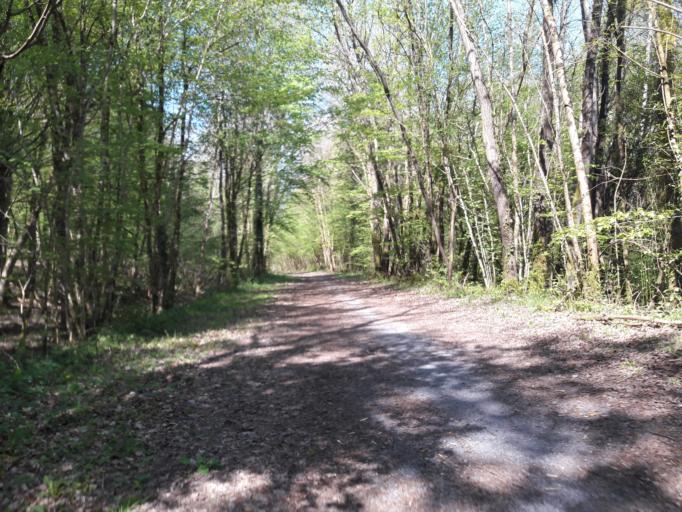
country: FR
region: Nord-Pas-de-Calais
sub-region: Departement du Nord
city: Sains-du-Nord
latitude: 50.1317
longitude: 4.0663
